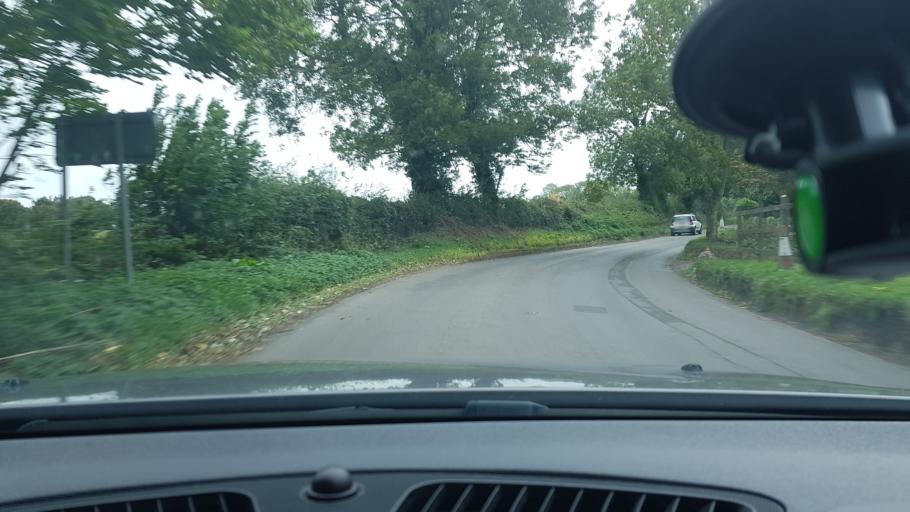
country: GB
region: England
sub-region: Wiltshire
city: Burbage
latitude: 51.3445
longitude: -1.6496
